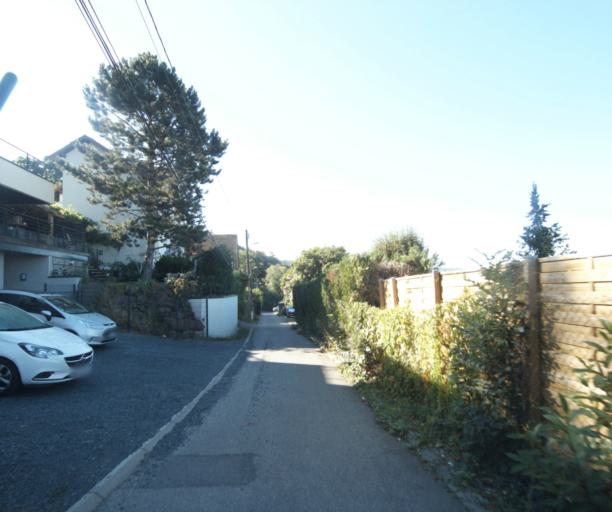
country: FR
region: Lorraine
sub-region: Departement des Vosges
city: Epinal
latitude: 48.1674
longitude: 6.4569
